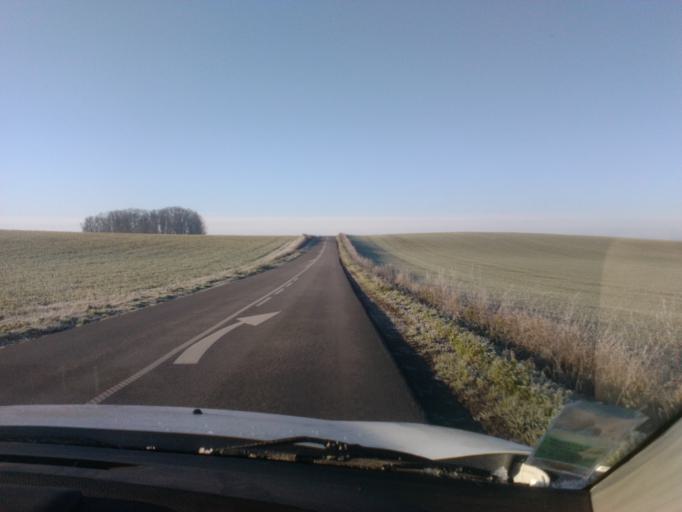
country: FR
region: Lorraine
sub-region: Departement des Vosges
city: Darnieulles
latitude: 48.1917
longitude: 6.2292
